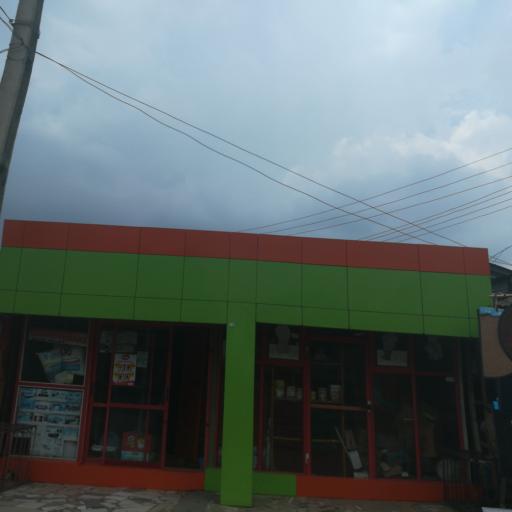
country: NG
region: Lagos
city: Ojota
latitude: 6.5851
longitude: 3.3842
